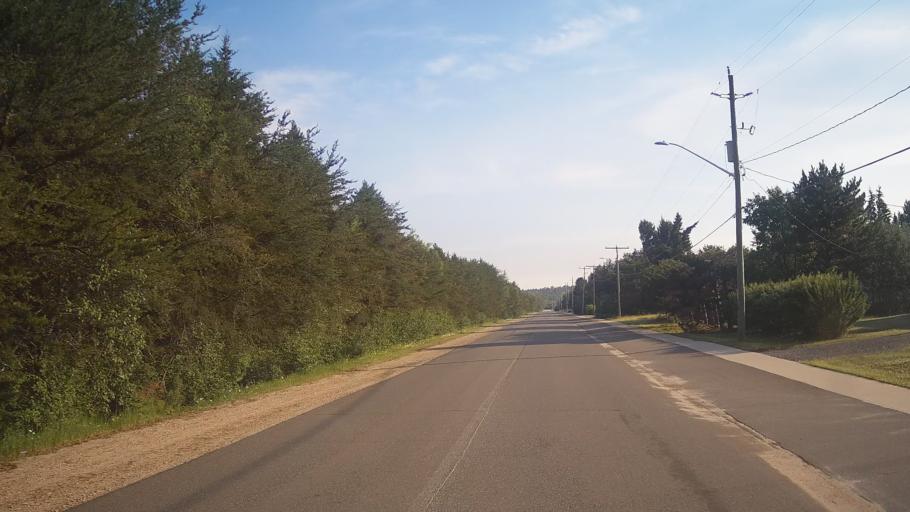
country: CA
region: Ontario
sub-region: Rainy River District
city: Atikokan
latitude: 49.4067
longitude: -91.6666
